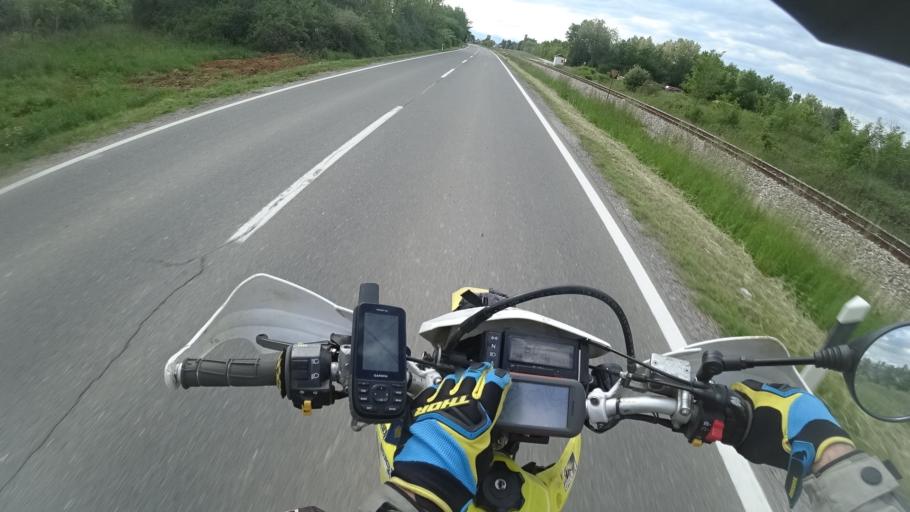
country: HR
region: Licko-Senjska
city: Gospic
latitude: 44.5270
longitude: 15.4087
